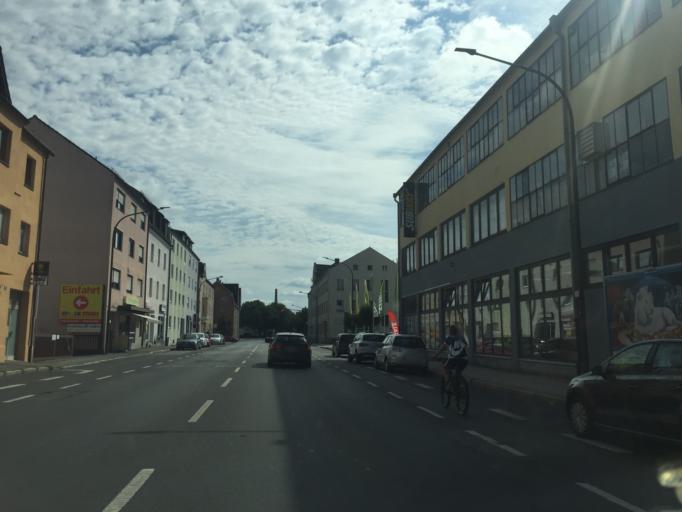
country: DE
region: Bavaria
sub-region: Upper Palatinate
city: Weiden
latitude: 49.6639
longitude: 12.1532
